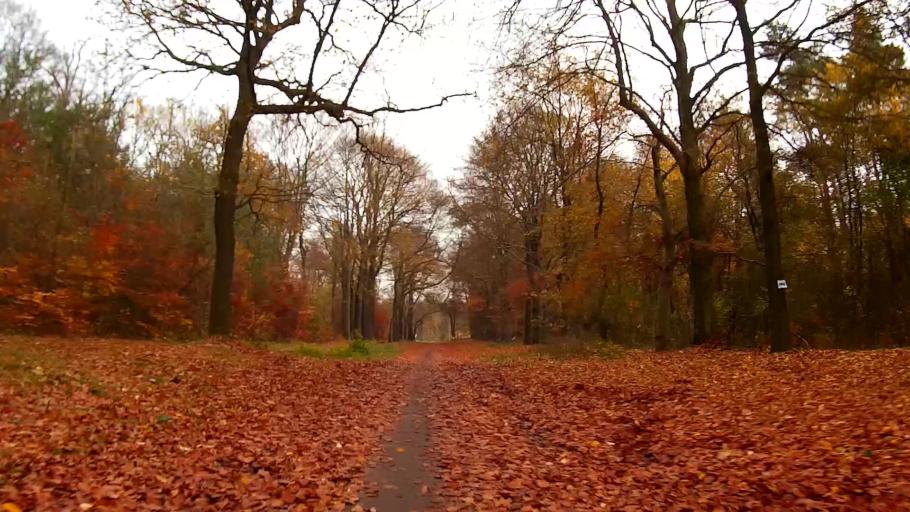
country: NL
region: Utrecht
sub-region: Gemeente Utrechtse Heuvelrug
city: Driebergen-Rijsenburg
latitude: 52.0971
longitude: 5.2962
